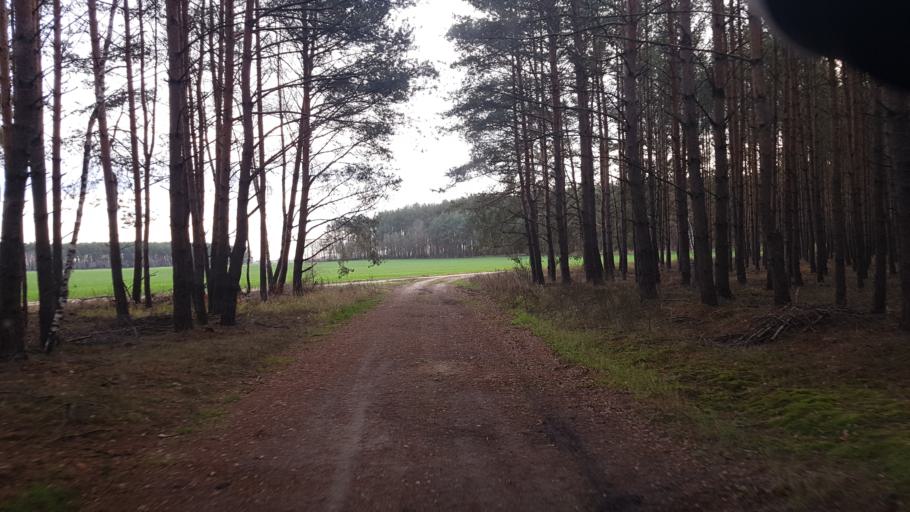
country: DE
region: Brandenburg
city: Hohenbucko
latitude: 51.7018
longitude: 13.5183
